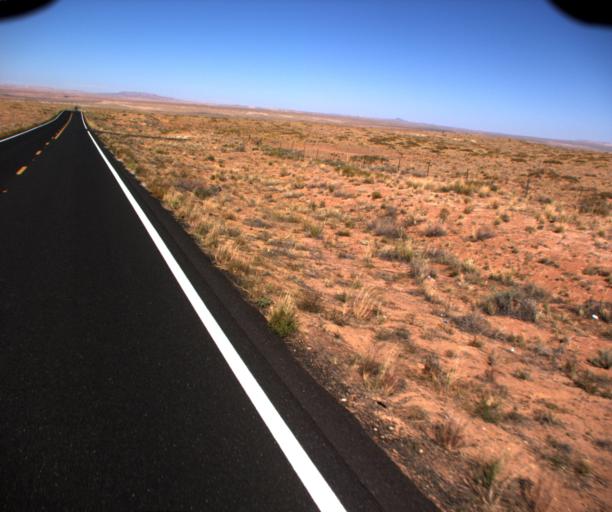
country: US
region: Arizona
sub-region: Coconino County
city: Tuba City
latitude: 36.0589
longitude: -111.1820
